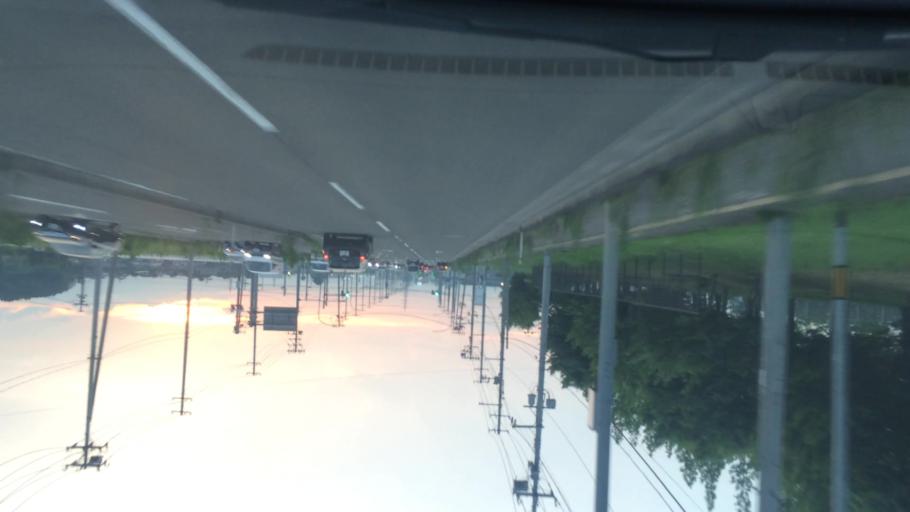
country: JP
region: Miyagi
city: Rifu
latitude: 38.3113
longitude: 140.9212
